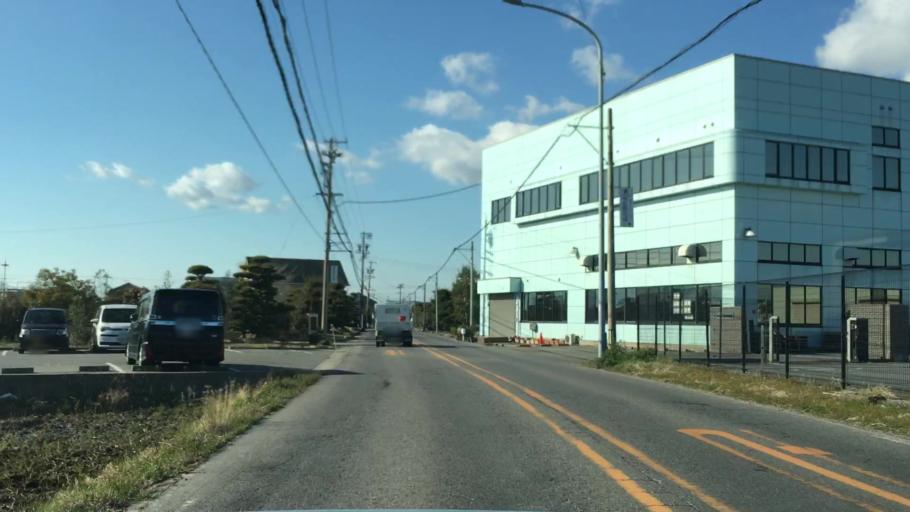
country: JP
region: Aichi
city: Nishio
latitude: 34.8443
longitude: 137.0476
